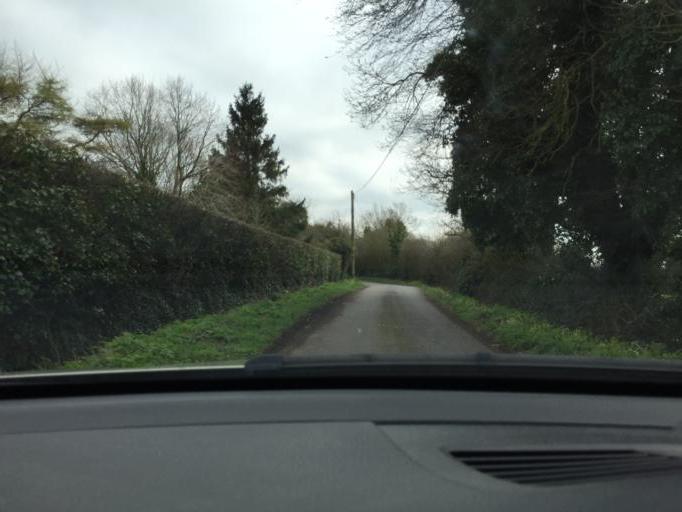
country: IE
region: Leinster
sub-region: An Mhi
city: Dunboyne
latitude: 53.4468
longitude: -6.4397
